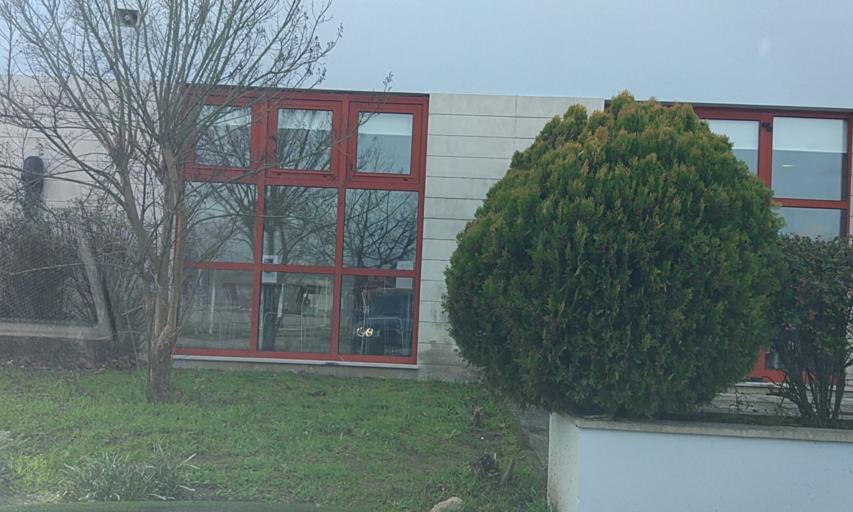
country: PT
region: Porto
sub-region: Maia
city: Pedroucos
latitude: 41.2013
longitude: -8.5690
